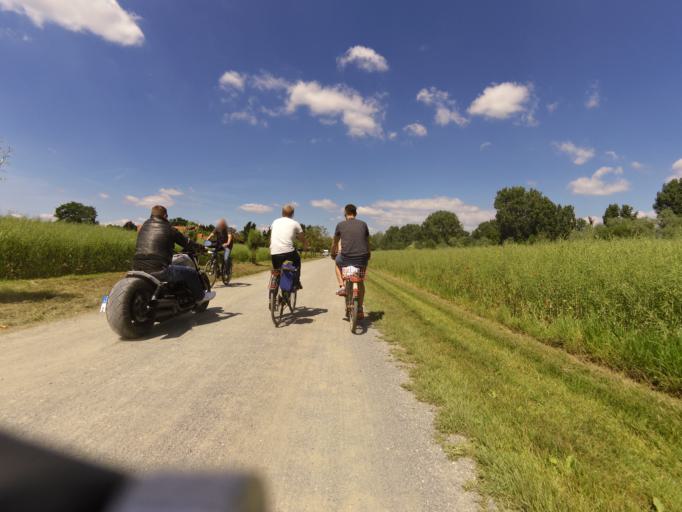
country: DE
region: Rheinland-Pfalz
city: Nackenheim
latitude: 49.9386
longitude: 8.3499
